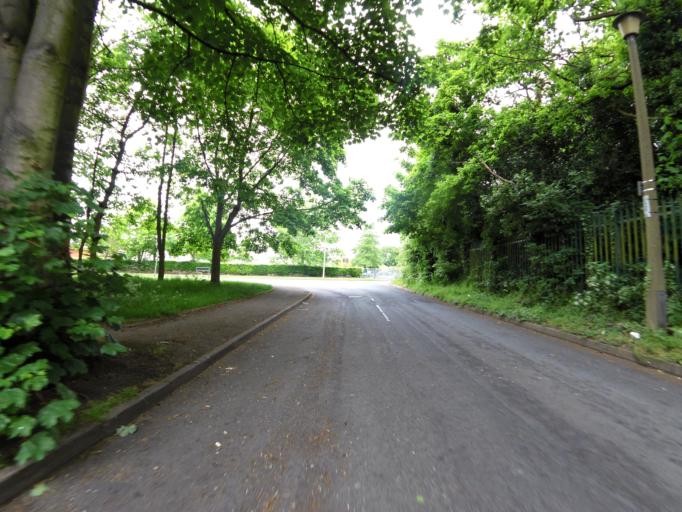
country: GB
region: England
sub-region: Suffolk
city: Ipswich
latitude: 52.0443
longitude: 1.1320
